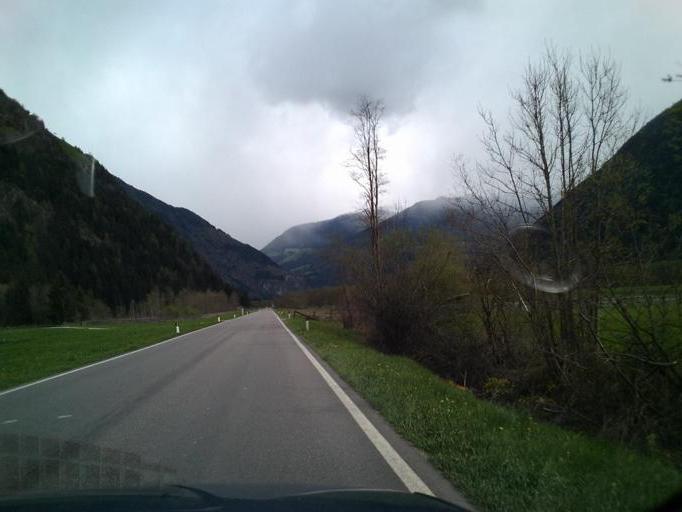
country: IT
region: Trentino-Alto Adige
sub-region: Bolzano
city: Molini di Tures
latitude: 46.8736
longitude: 11.9481
